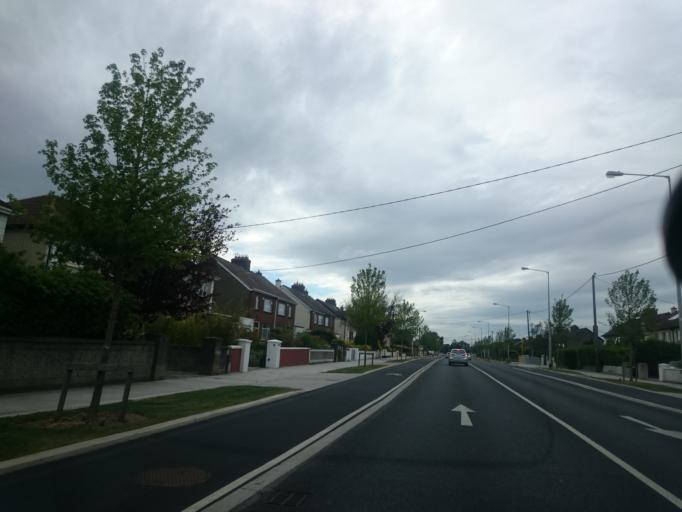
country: IE
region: Leinster
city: Dundrum
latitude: 53.2993
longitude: -6.2605
